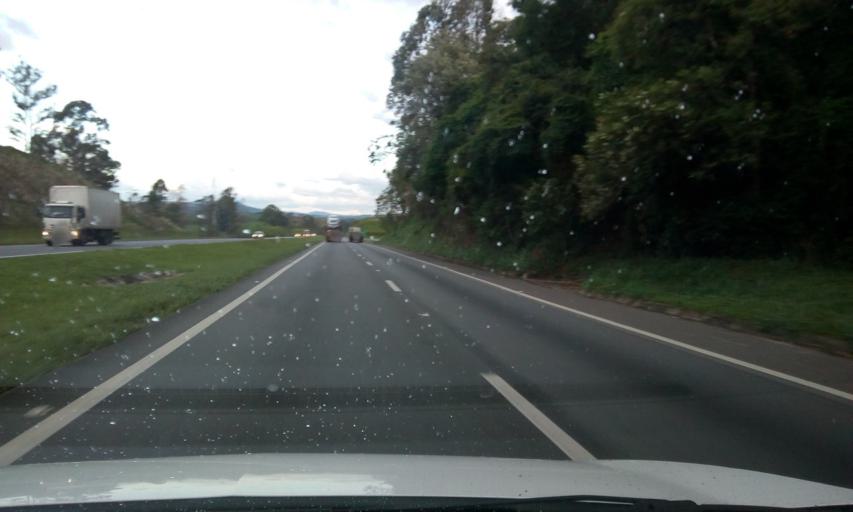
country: BR
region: Sao Paulo
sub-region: Jarinu
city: Jarinu
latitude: -23.0358
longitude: -46.7223
